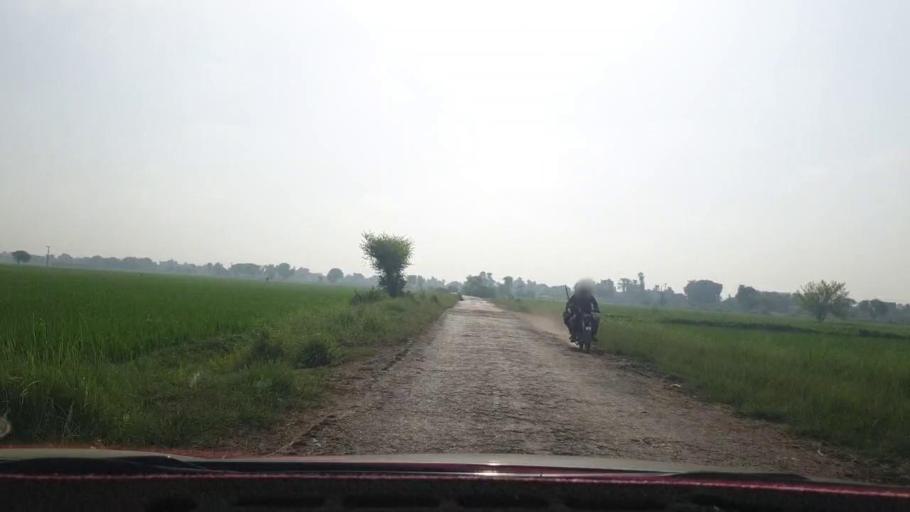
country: PK
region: Sindh
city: Nasirabad
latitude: 27.4556
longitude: 67.9580
